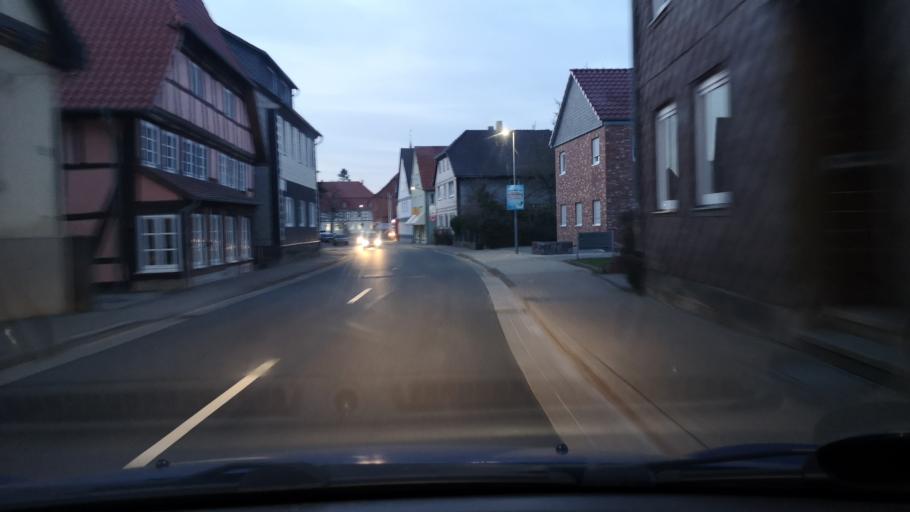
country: DE
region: Lower Saxony
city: Coppenbrugge
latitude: 52.1182
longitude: 9.5495
